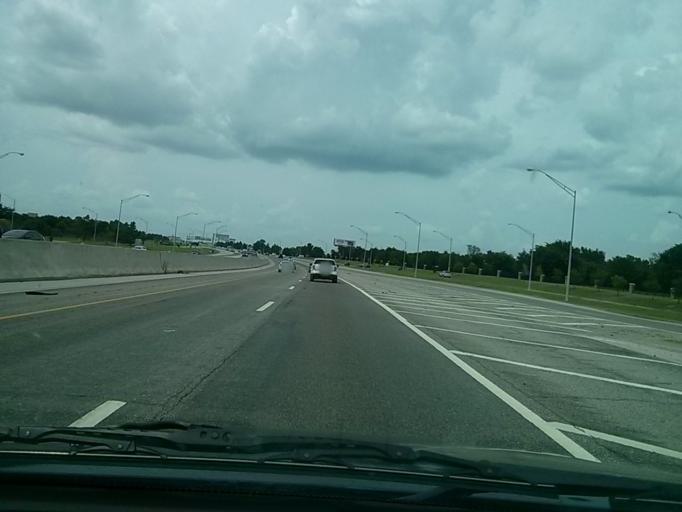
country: US
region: Oklahoma
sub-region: Tulsa County
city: Broken Arrow
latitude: 36.0334
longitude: -95.8597
